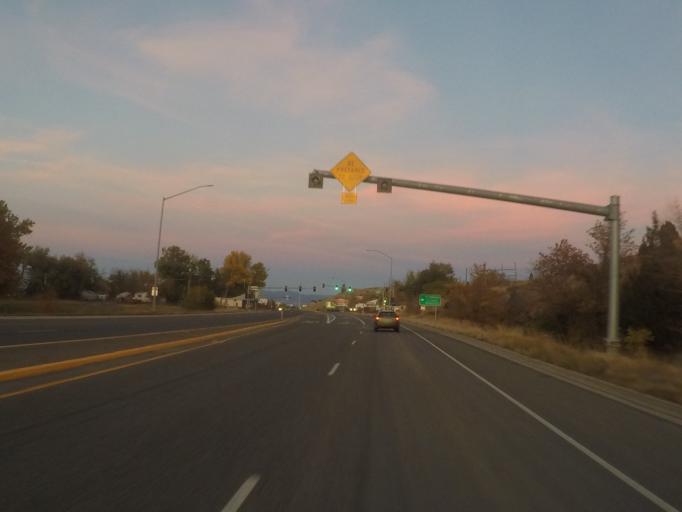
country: US
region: Montana
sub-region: Lewis and Clark County
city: Helena West Side
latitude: 46.6020
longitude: -112.0909
